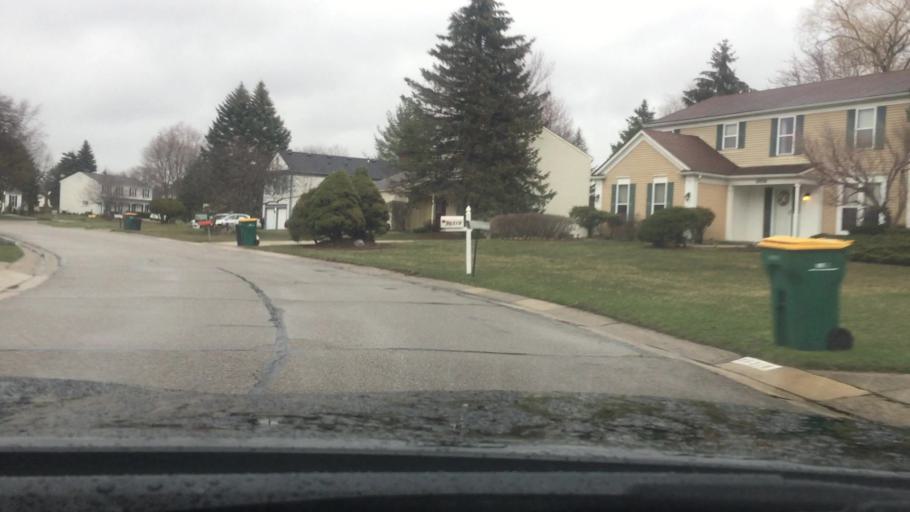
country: US
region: Michigan
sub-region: Oakland County
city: Farmington Hills
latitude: 42.4991
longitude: -83.4051
